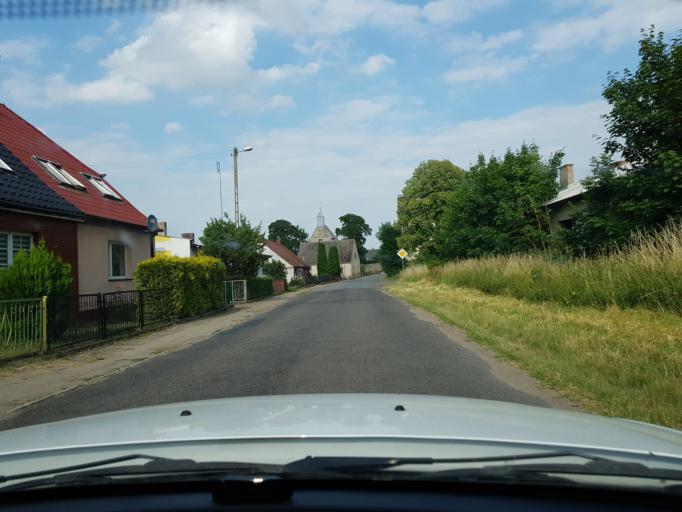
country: PL
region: West Pomeranian Voivodeship
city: Trzcinsko Zdroj
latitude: 53.0182
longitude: 14.5562
